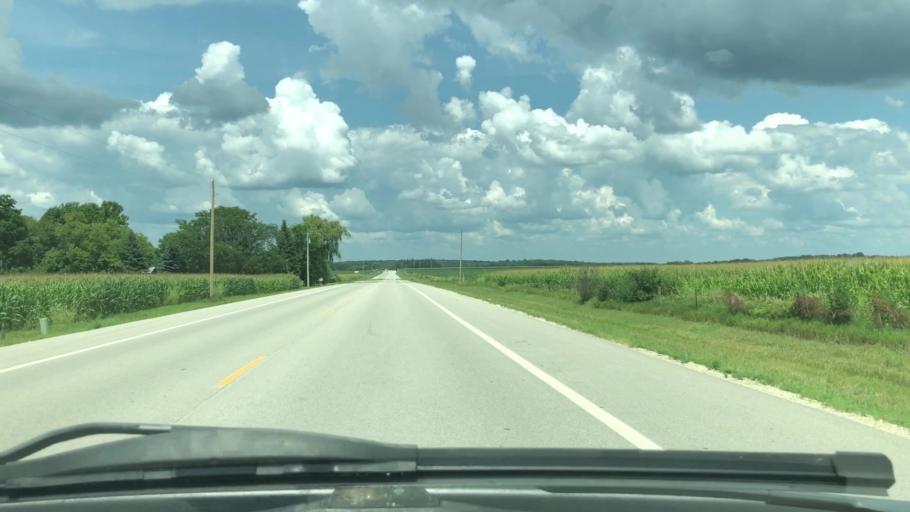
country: US
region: Minnesota
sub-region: Olmsted County
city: Rochester
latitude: 43.9553
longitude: -92.5184
